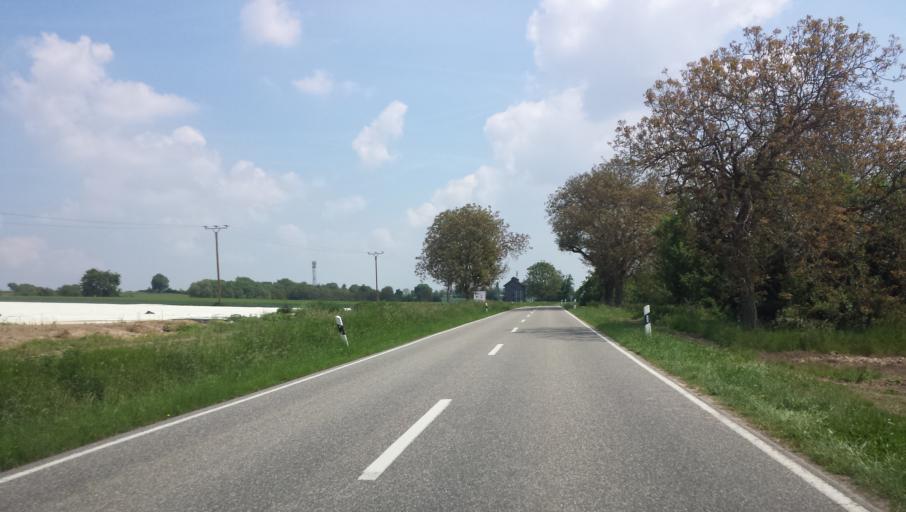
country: DE
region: Rheinland-Pfalz
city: Kapsweyer
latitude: 49.0453
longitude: 8.0151
